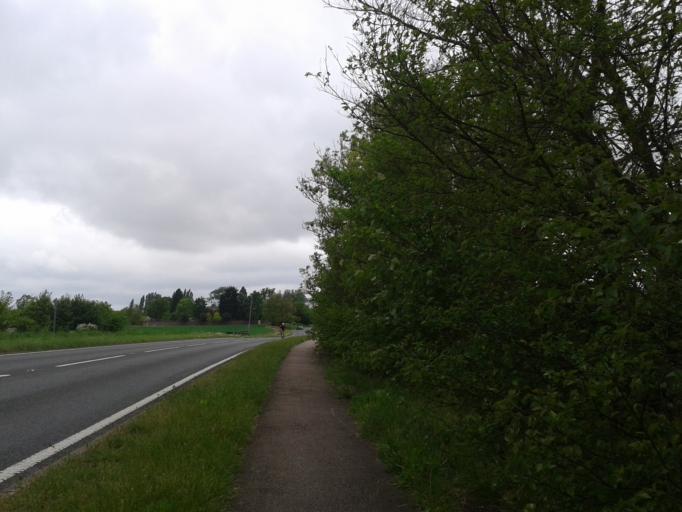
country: GB
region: England
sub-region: Cambridgeshire
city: Great Stukeley
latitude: 52.3492
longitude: -0.2029
